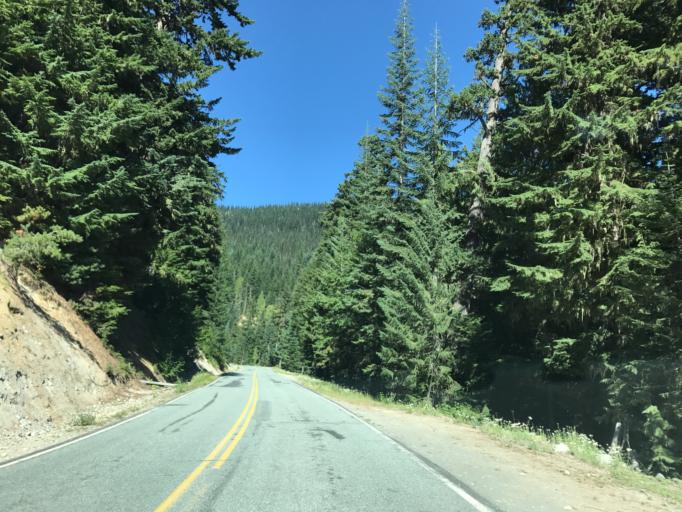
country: US
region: Washington
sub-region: King County
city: Enumclaw
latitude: 46.9086
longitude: -121.5786
